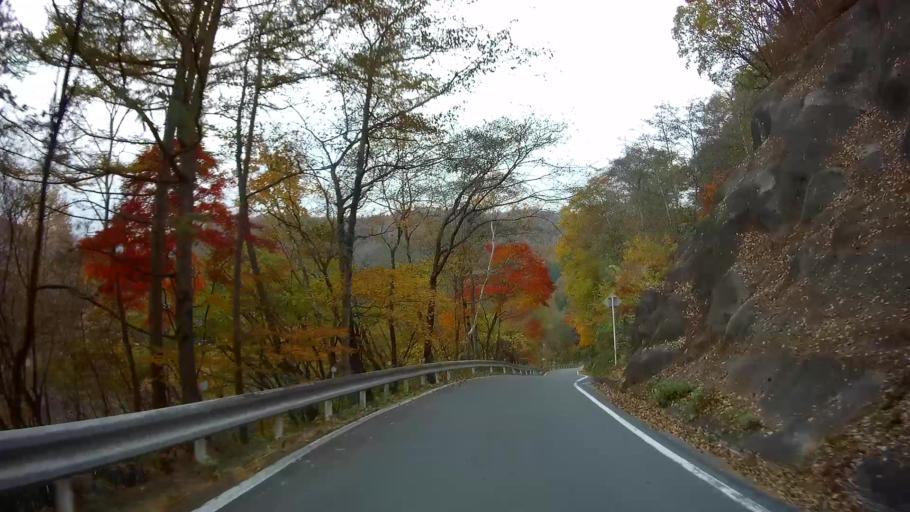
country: JP
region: Gunma
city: Nakanojomachi
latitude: 36.6537
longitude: 138.6596
